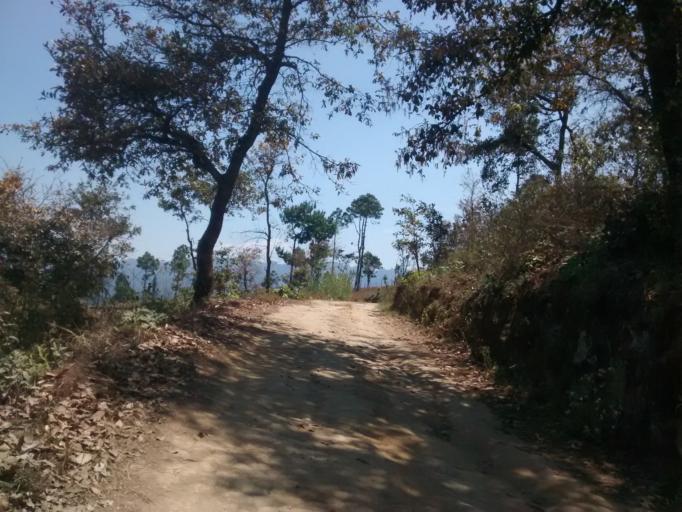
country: GT
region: Sacatepequez
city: Sumpango
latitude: 14.6712
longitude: -90.7313
